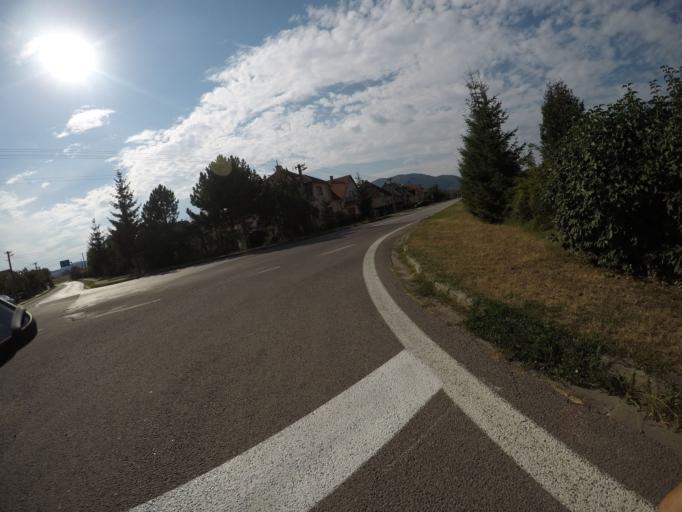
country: SK
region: Trenciansky
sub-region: Okres Trencin
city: Trencin
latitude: 48.8771
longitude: 17.9688
